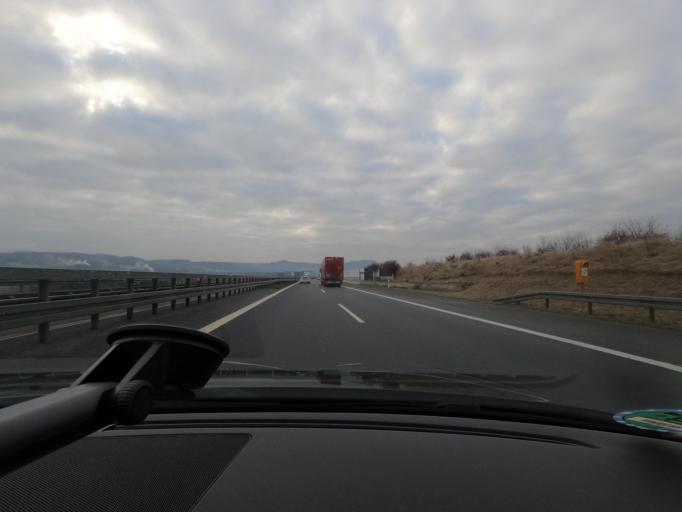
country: DE
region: Bavaria
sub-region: Upper Franconia
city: Lichtenfels
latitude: 50.1348
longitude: 11.0351
